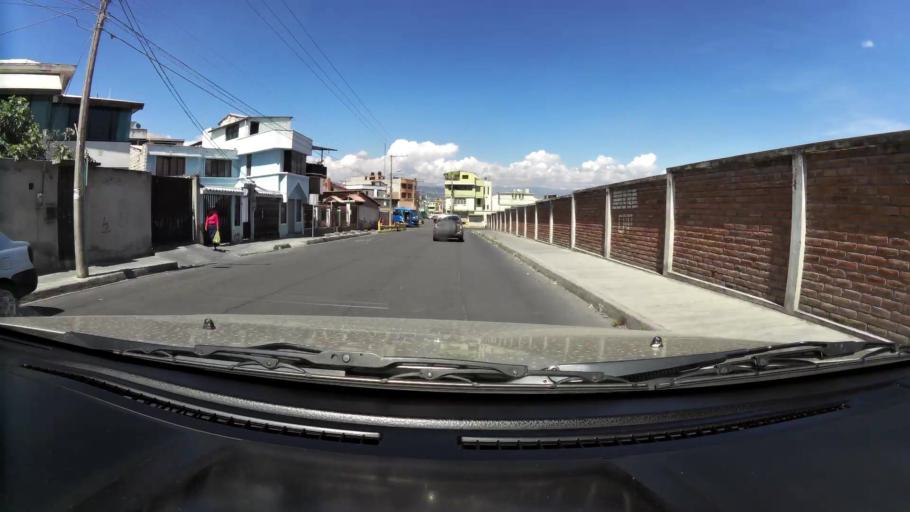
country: EC
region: Chimborazo
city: Riobamba
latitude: -1.6816
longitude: -78.6324
